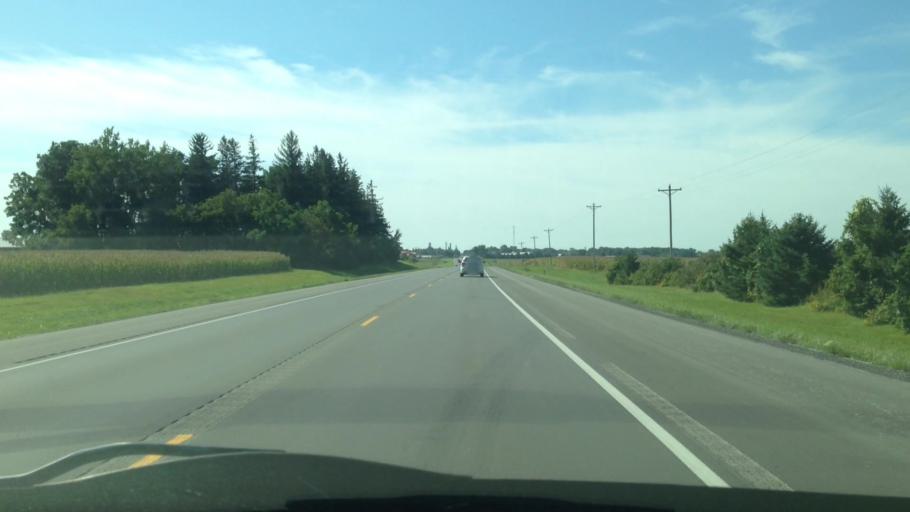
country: US
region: Minnesota
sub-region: Fillmore County
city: Harmony
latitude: 43.5779
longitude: -92.0101
